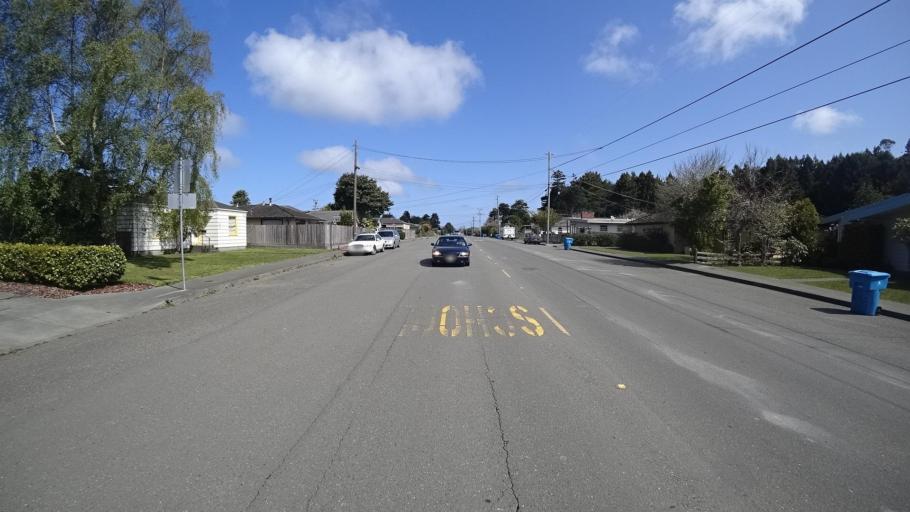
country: US
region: California
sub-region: Humboldt County
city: Cutten
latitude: 40.7719
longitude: -124.1615
